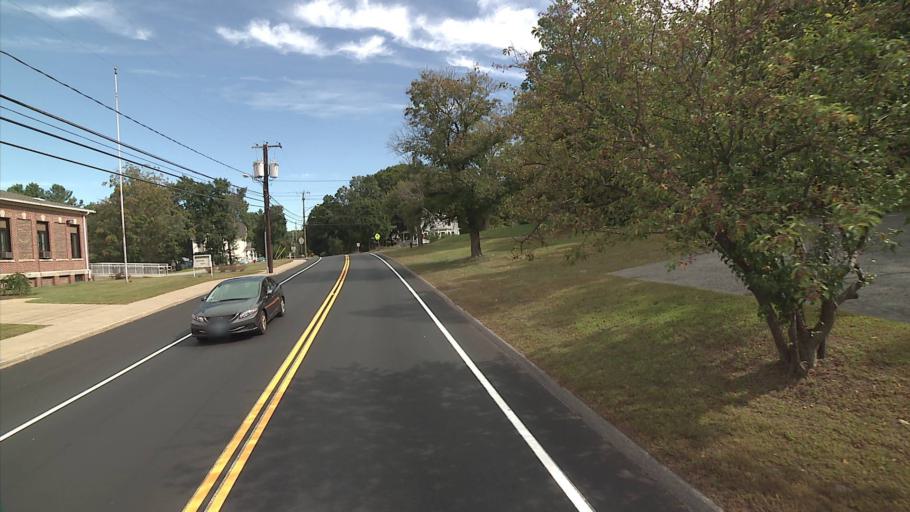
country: US
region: Connecticut
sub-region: Tolland County
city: Storrs
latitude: 41.8512
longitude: -72.3018
